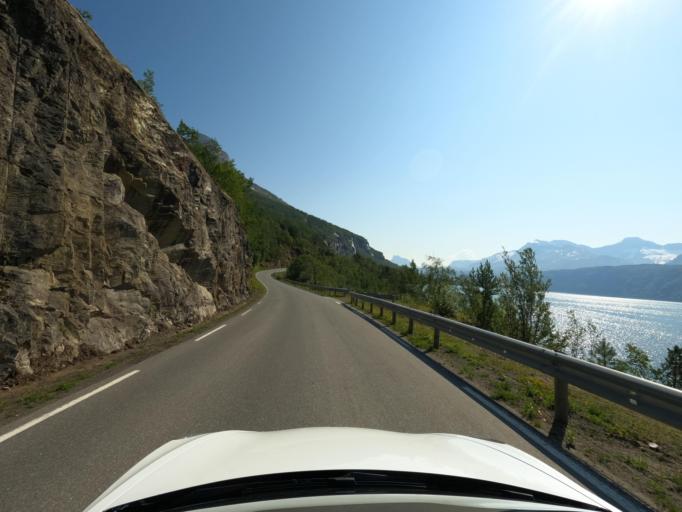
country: NO
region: Nordland
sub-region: Narvik
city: Narvik
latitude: 68.3571
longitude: 17.2703
